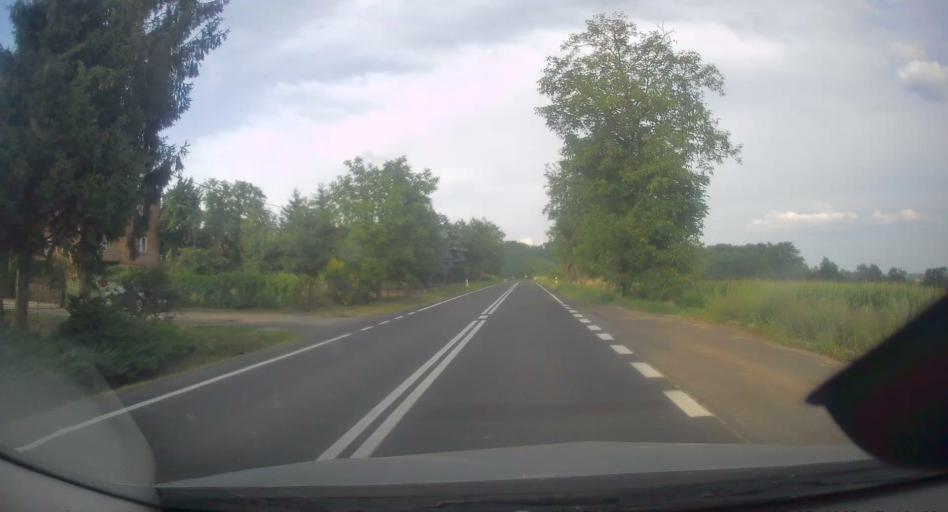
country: PL
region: Lesser Poland Voivodeship
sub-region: Powiat bochenski
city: Dziewin
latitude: 50.1452
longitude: 20.5116
